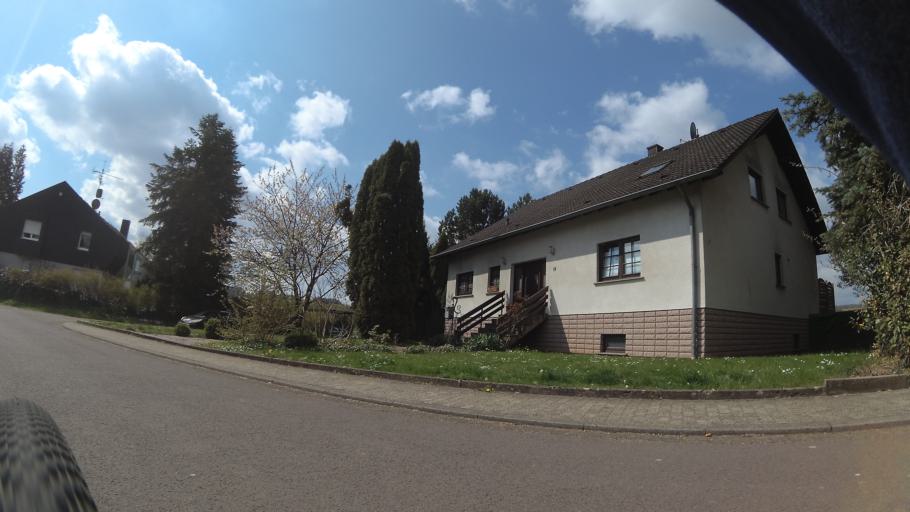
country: DE
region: Saarland
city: Schmelz
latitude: 49.4898
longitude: 6.8351
